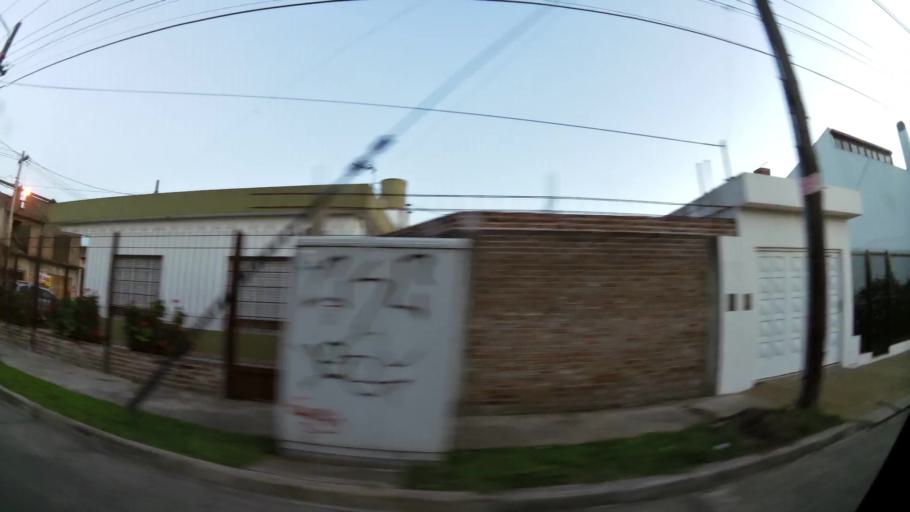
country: AR
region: Buenos Aires
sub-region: Partido de Quilmes
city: Quilmes
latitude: -34.7747
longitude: -58.2102
